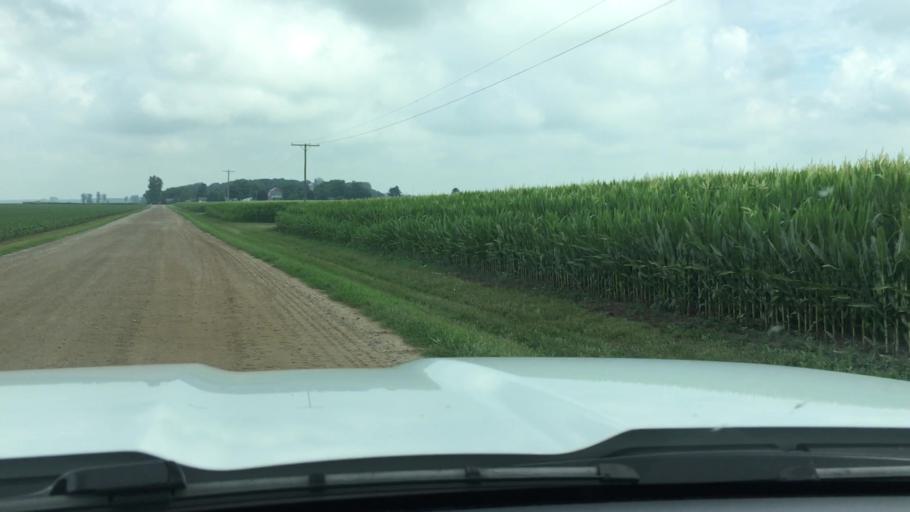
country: US
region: Michigan
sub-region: Sanilac County
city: Marlette
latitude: 43.3525
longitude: -82.9756
